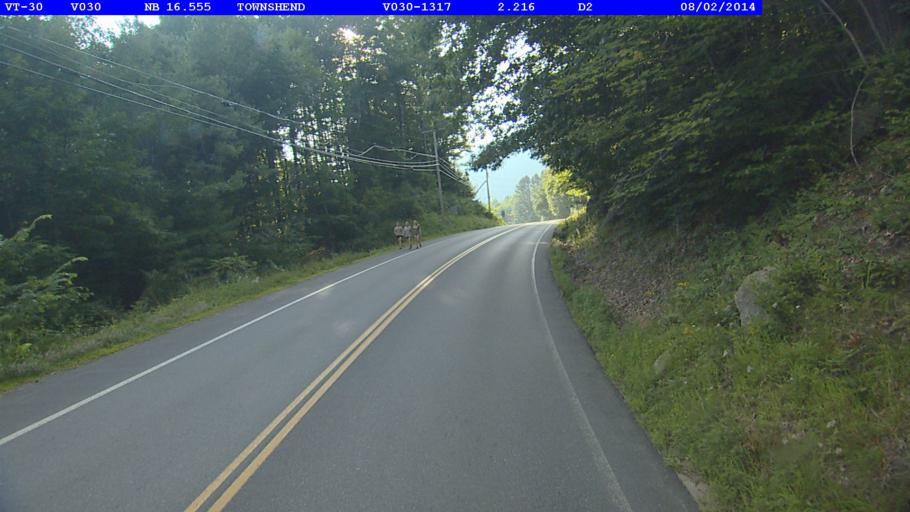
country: US
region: Vermont
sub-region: Windham County
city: Newfane
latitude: 43.0461
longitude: -72.6713
